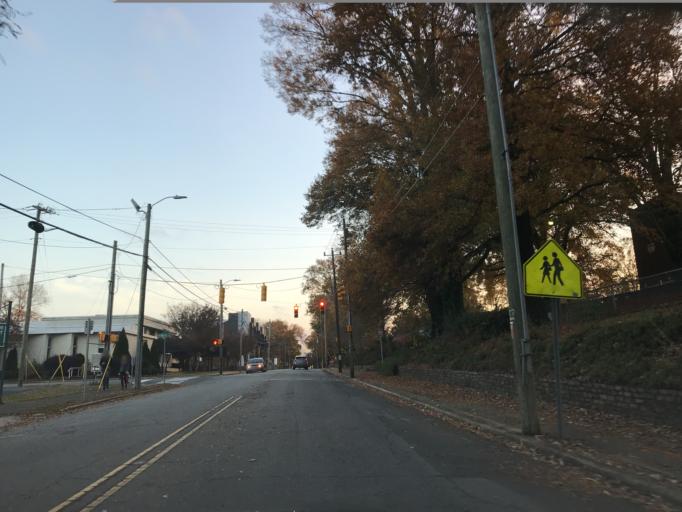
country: US
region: North Carolina
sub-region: Wake County
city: West Raleigh
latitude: 35.7855
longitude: -78.6507
